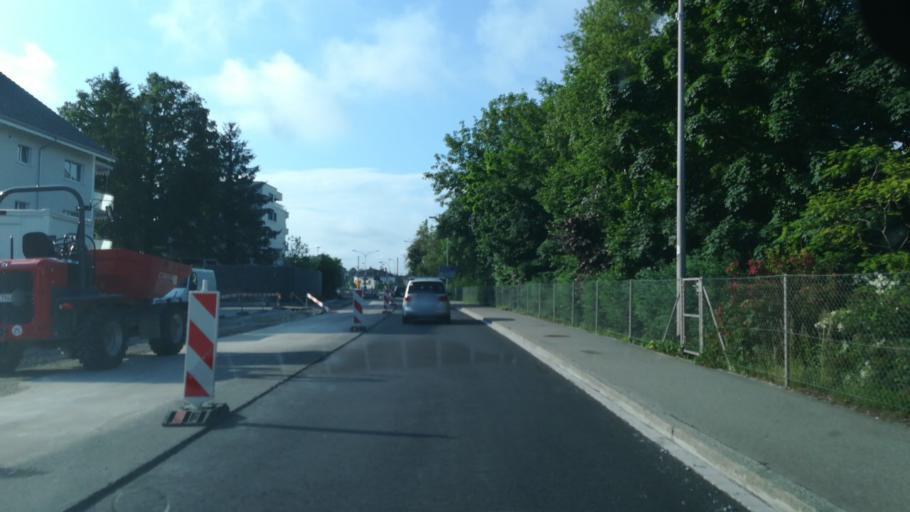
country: CH
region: Thurgau
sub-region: Weinfelden District
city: Sulgen
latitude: 47.5401
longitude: 9.1834
